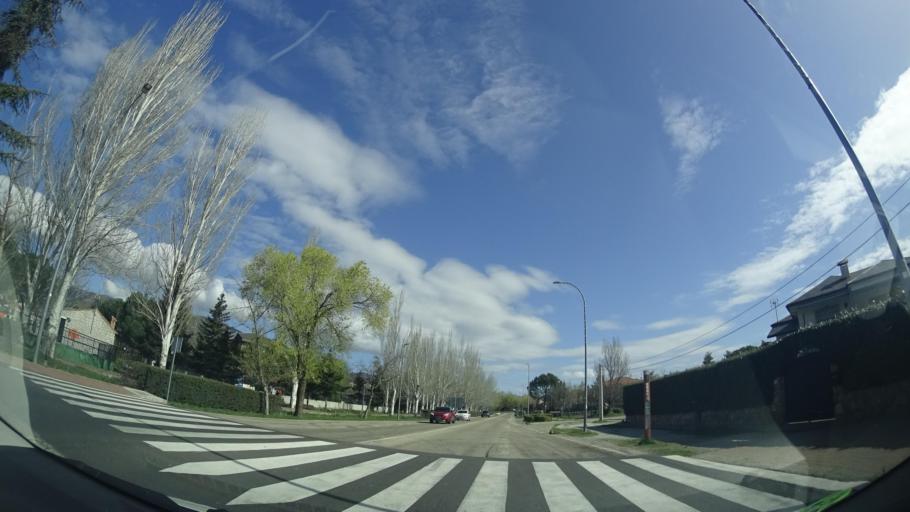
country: ES
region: Madrid
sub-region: Provincia de Madrid
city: Miraflores de la Sierra
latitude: 40.7497
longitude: -3.7828
